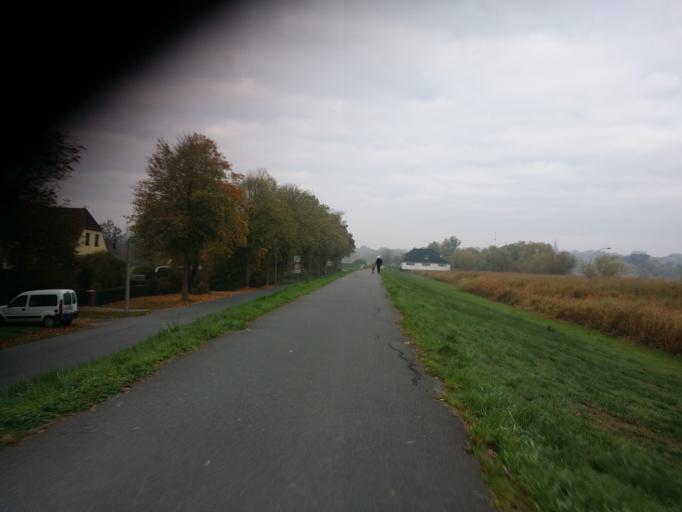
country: DE
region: Lower Saxony
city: Ritterhude
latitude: 53.1585
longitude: 8.6990
